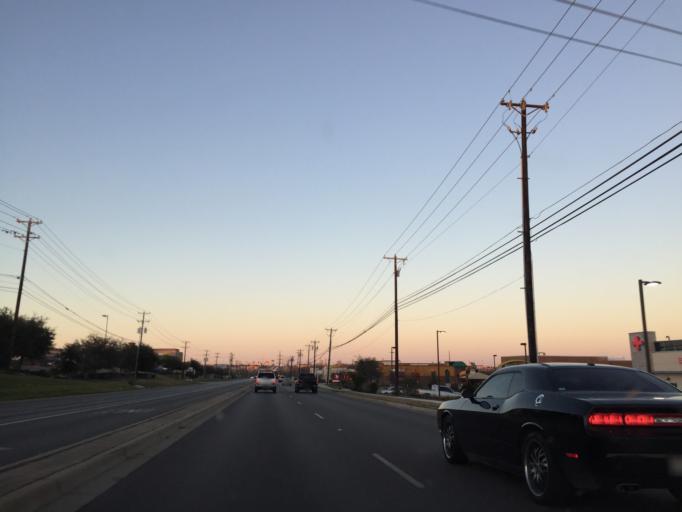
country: US
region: Texas
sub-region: Travis County
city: Pflugerville
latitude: 30.4508
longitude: -97.6050
